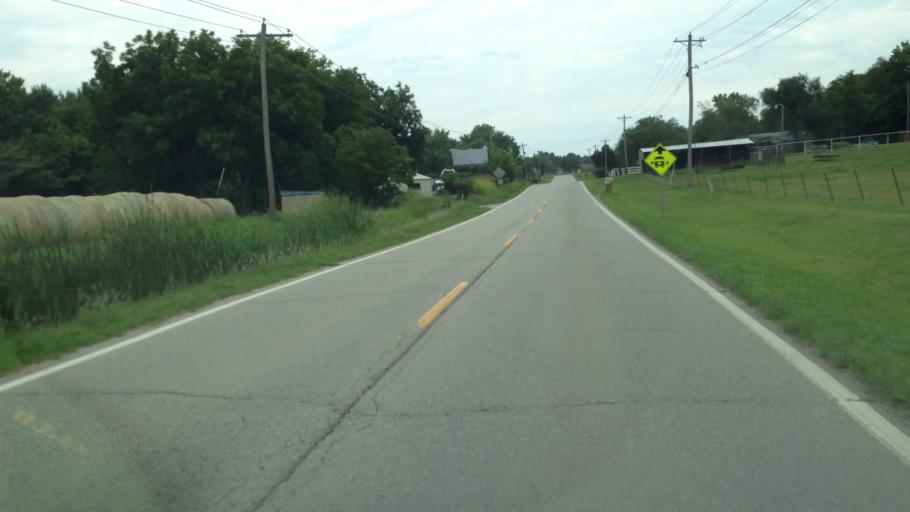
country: US
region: Oklahoma
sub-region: Delaware County
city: Cleora
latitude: 36.5762
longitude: -94.9707
